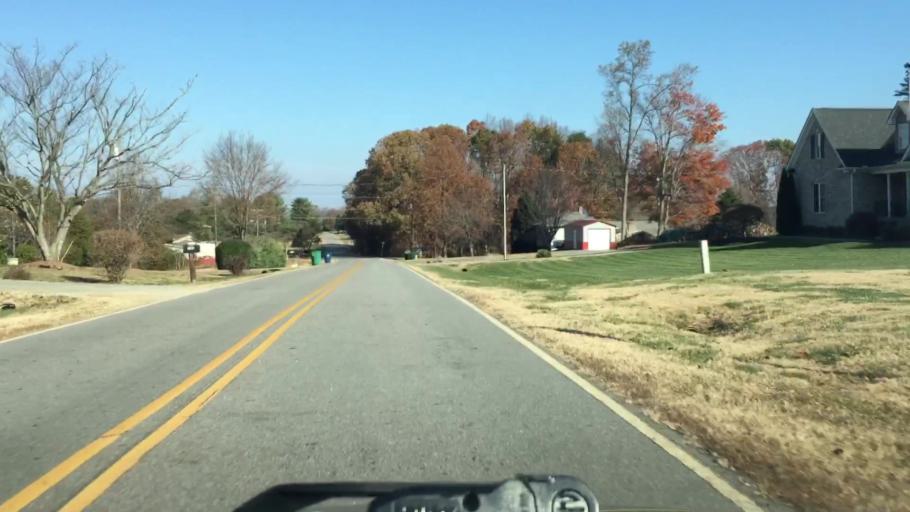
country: US
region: North Carolina
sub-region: Rockingham County
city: Reidsville
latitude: 36.3365
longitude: -79.6140
